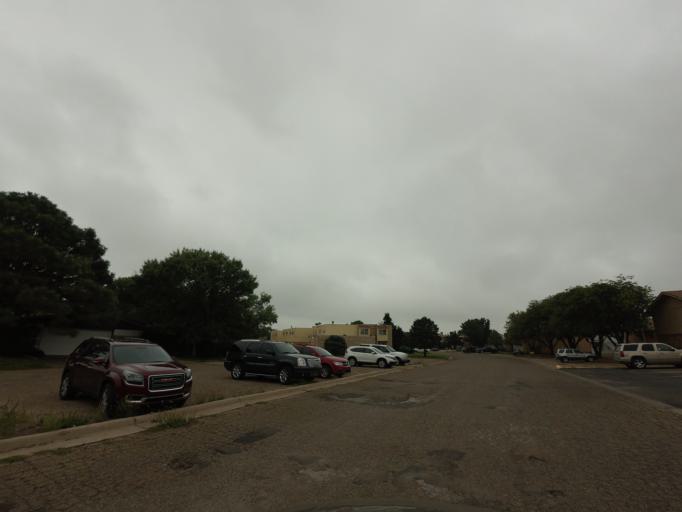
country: US
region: New Mexico
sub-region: Curry County
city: Clovis
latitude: 34.4390
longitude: -103.1950
